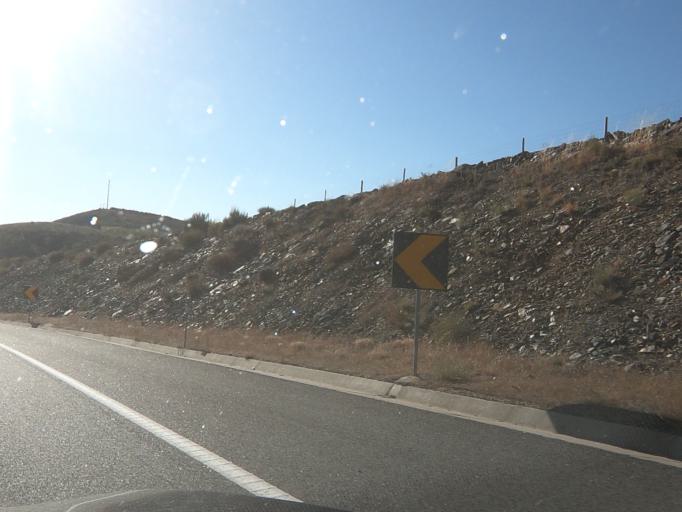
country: PT
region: Vila Real
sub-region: Murca
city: Murca
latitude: 41.4284
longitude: -7.3574
